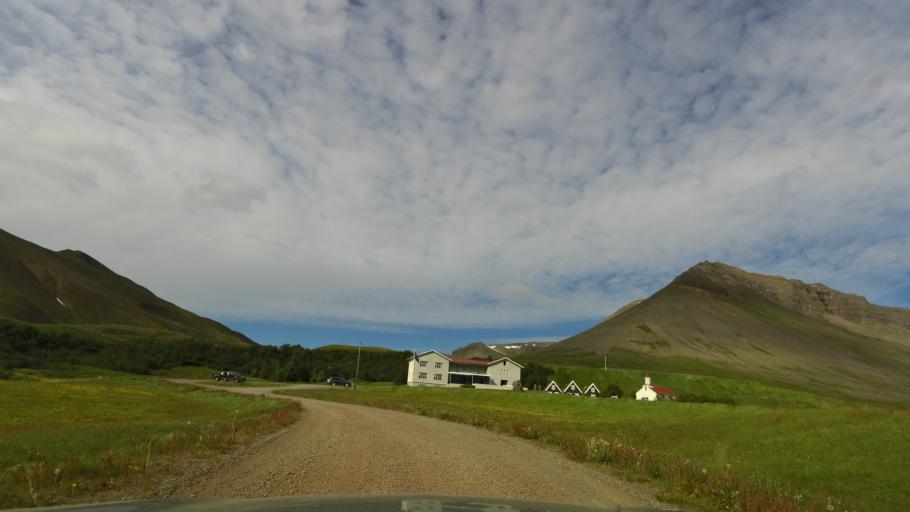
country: IS
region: Westfjords
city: Isafjoerdur
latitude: 65.7588
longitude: -23.4524
